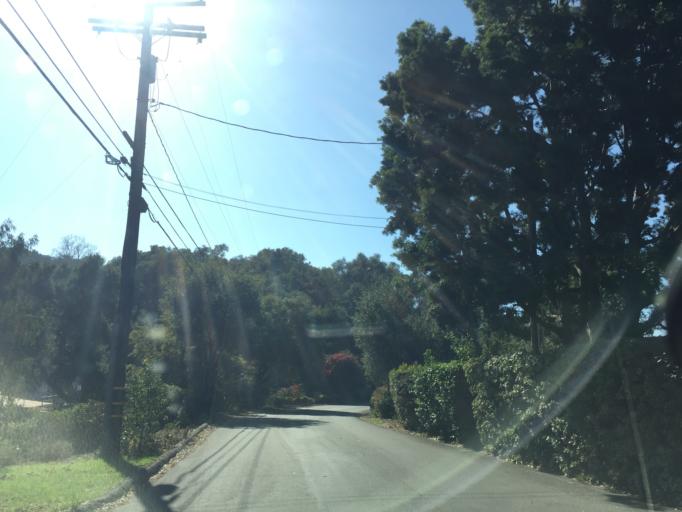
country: US
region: California
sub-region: Santa Barbara County
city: Goleta
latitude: 34.4340
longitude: -119.7721
